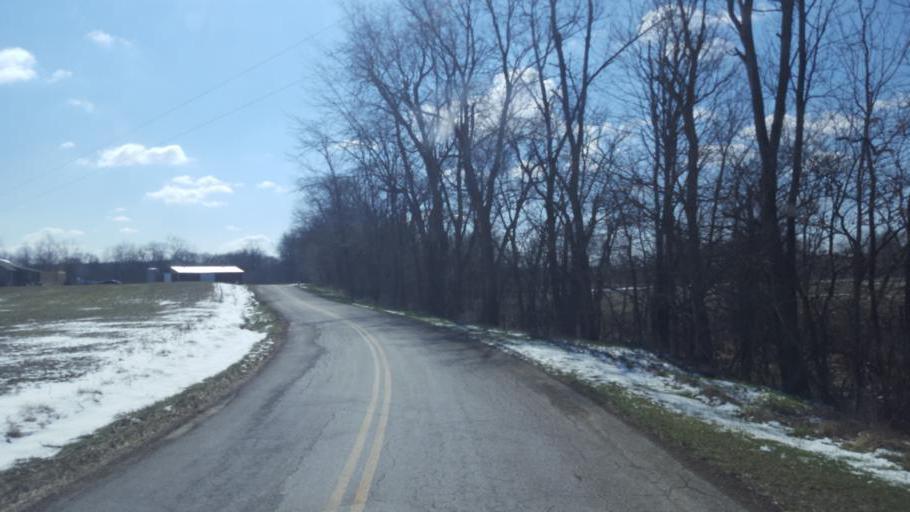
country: US
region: Ohio
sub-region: Licking County
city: Utica
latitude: 40.2644
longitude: -82.4614
